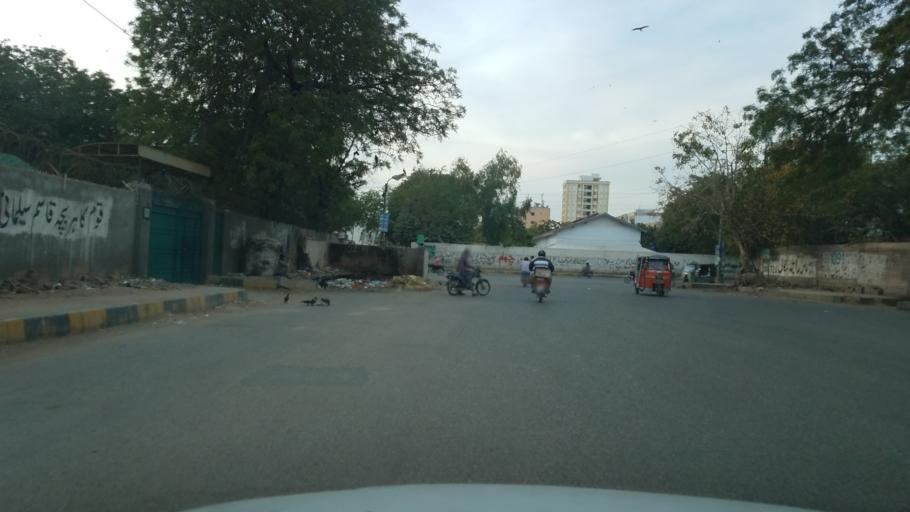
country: PK
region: Sindh
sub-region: Karachi District
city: Karachi
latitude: 24.8682
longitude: 67.0274
